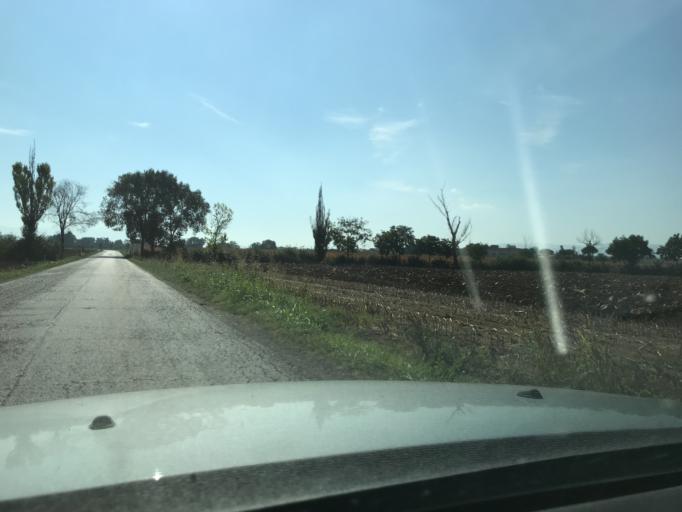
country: IT
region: Umbria
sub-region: Provincia di Perugia
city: Ospedalicchio
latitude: 43.0885
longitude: 12.5051
